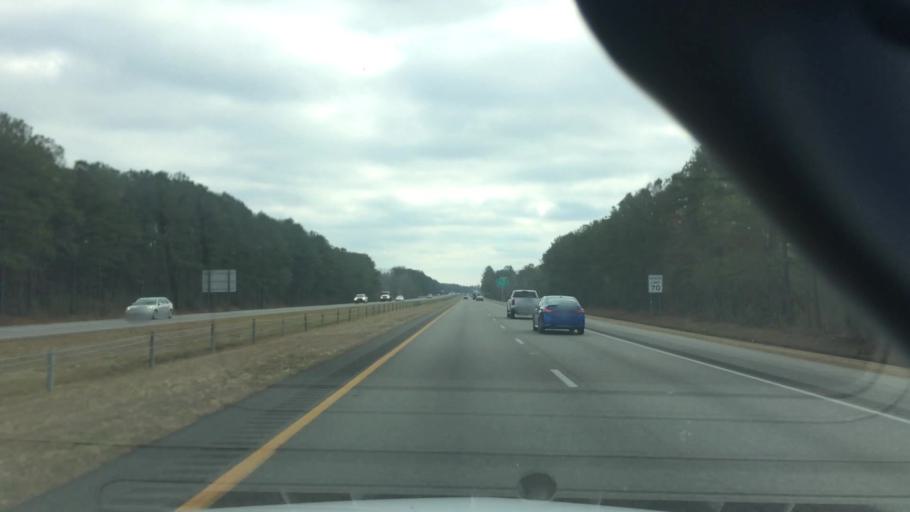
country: US
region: North Carolina
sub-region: New Hanover County
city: Skippers Corner
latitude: 34.3436
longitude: -77.8807
